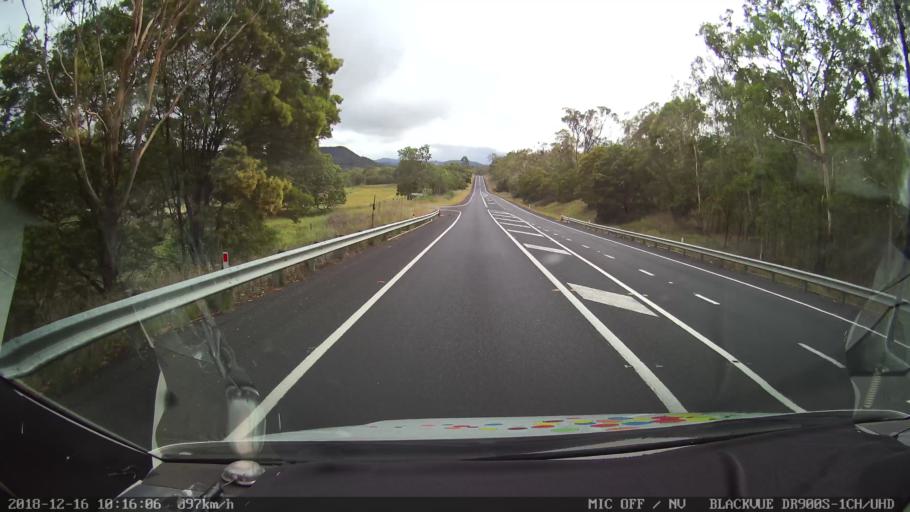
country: AU
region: New South Wales
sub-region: Tenterfield Municipality
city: Carrolls Creek
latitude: -29.2703
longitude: 151.9791
